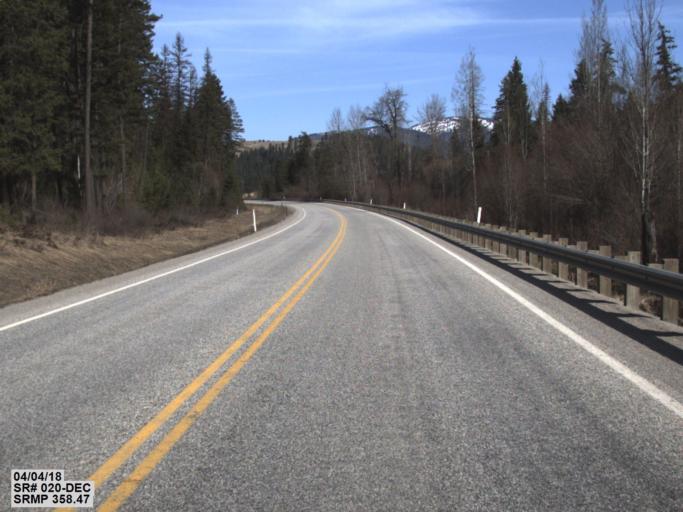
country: US
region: Washington
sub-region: Stevens County
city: Colville
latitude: 48.5360
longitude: -117.8230
